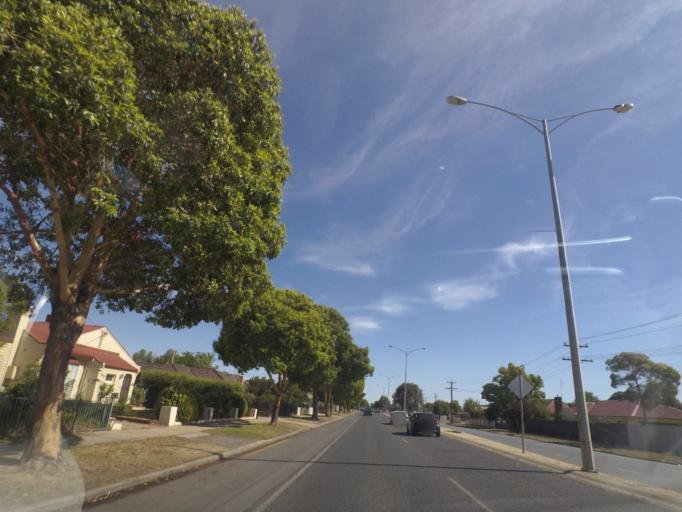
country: AU
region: Victoria
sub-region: Greater Shepparton
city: Shepparton
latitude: -36.3928
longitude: 145.3970
